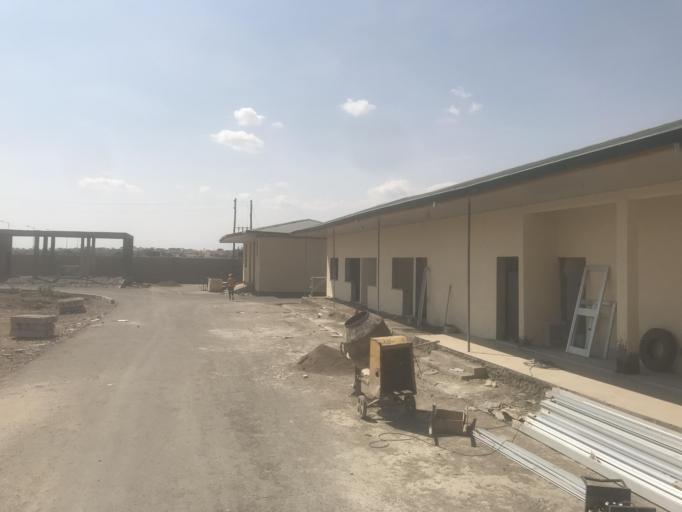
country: ET
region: Oromiya
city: Ziway
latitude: 8.1453
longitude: 38.7968
